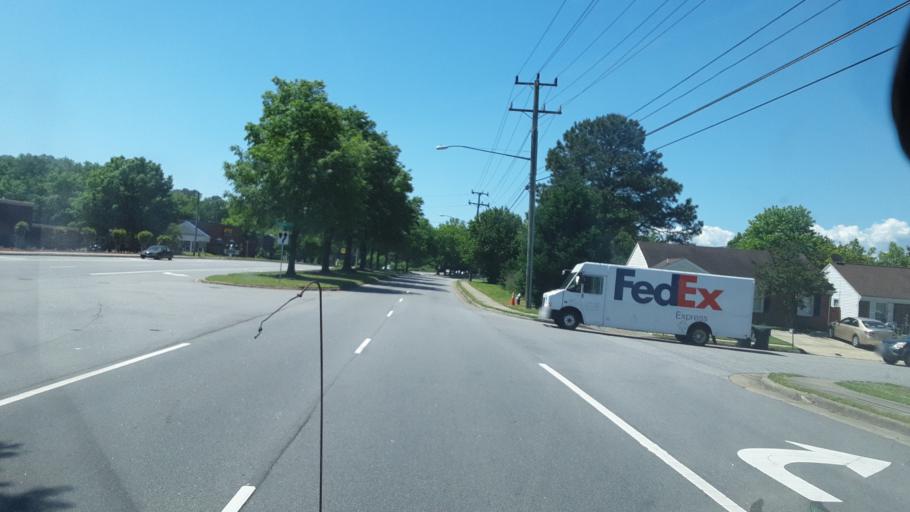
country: US
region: Virginia
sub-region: City of Virginia Beach
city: Virginia Beach
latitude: 36.7811
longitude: -76.0021
